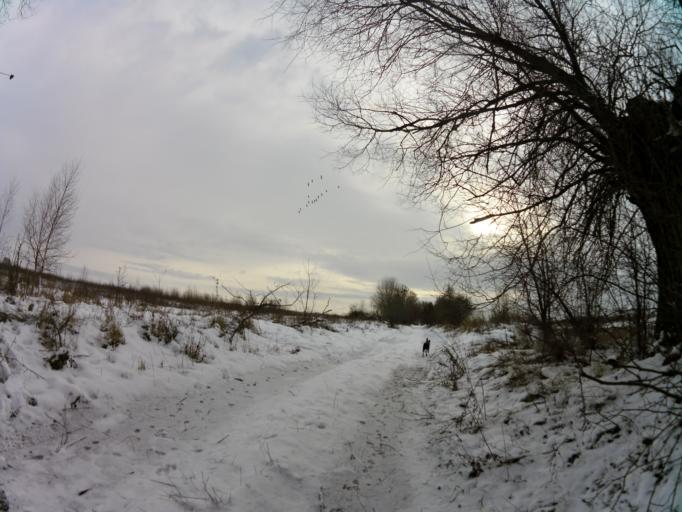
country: PL
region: West Pomeranian Voivodeship
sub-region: Powiat choszczenski
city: Recz
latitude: 53.2874
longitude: 15.5056
